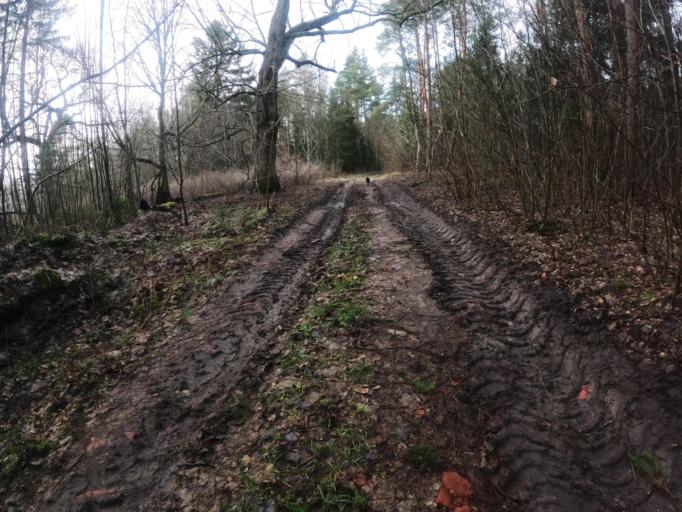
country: PL
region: West Pomeranian Voivodeship
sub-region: Powiat slawienski
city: Slawno
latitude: 54.2454
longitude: 16.6888
